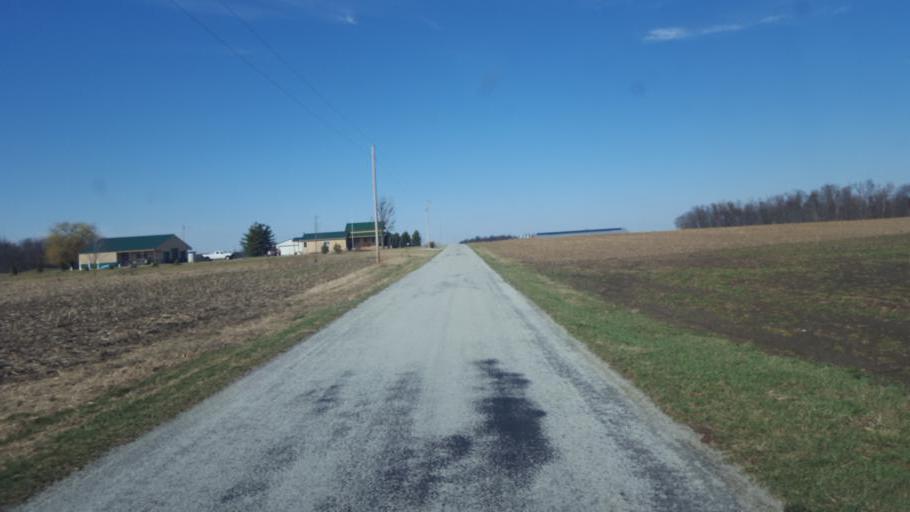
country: US
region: Ohio
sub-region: Hardin County
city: Forest
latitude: 40.6759
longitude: -83.4400
